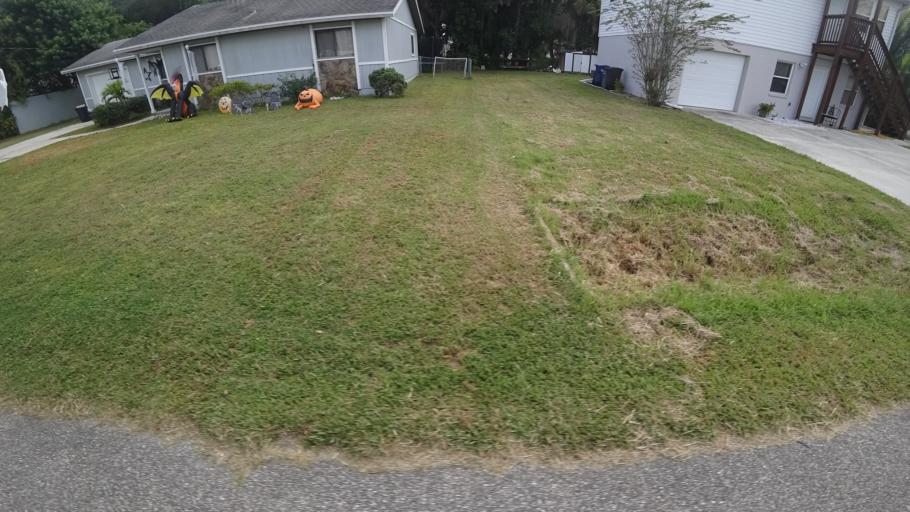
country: US
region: Florida
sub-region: Manatee County
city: Memphis
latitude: 27.5479
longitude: -82.5691
